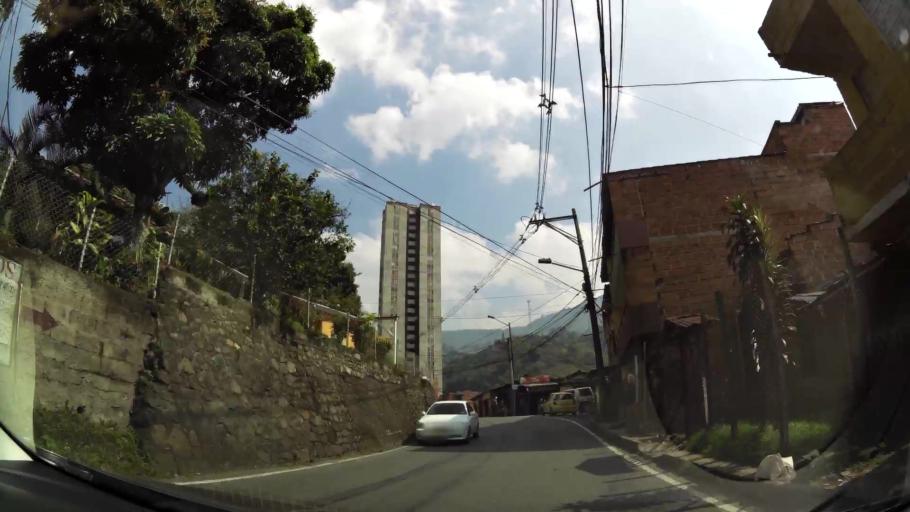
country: CO
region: Antioquia
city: La Estrella
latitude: 6.1785
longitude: -75.6381
